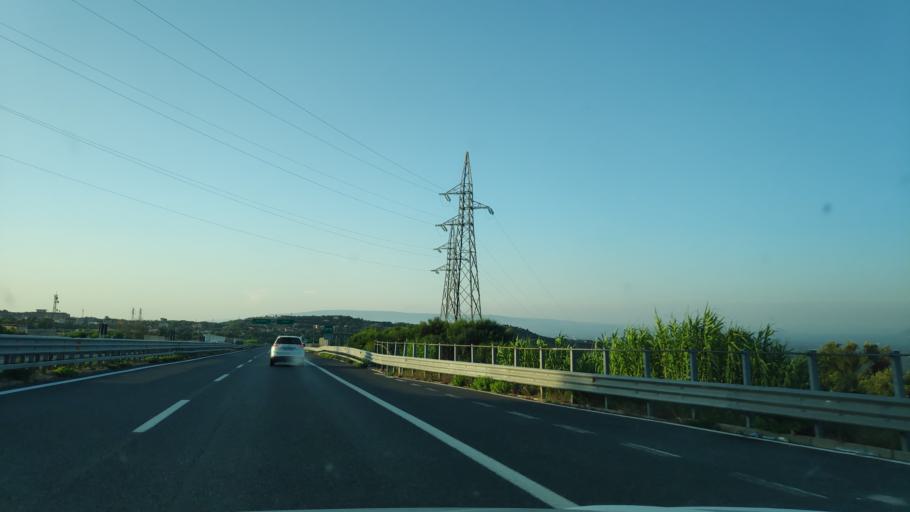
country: IT
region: Calabria
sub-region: Provincia di Reggio Calabria
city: Seminara
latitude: 38.3615
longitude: 15.8651
